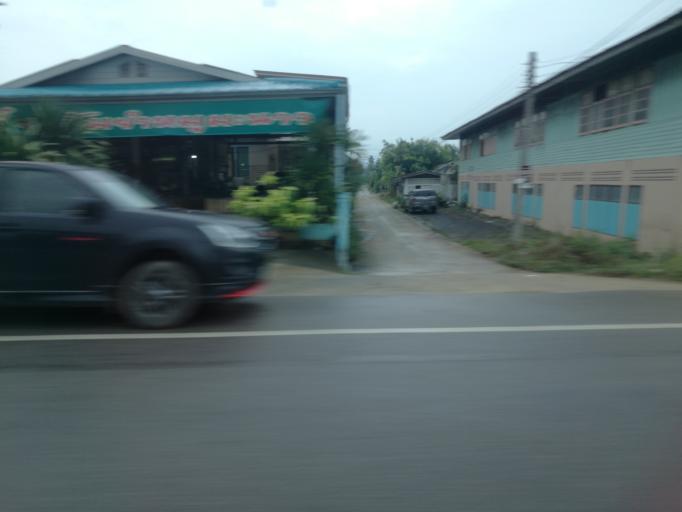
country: TH
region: Prachuap Khiri Khan
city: Kui Buri
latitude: 12.0374
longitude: 99.8461
